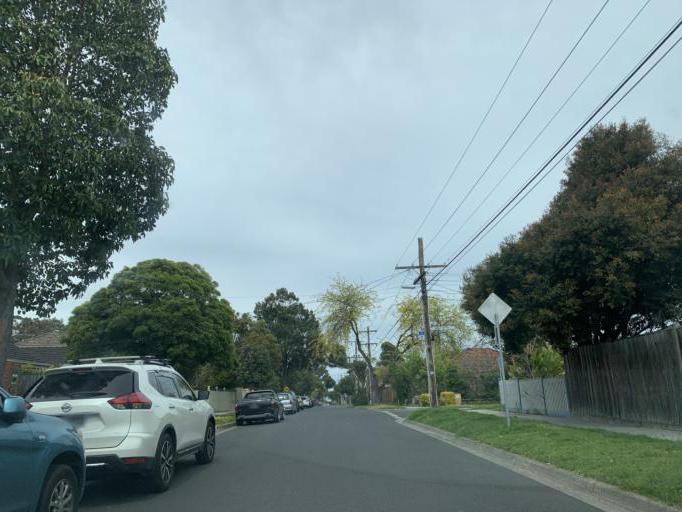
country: AU
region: Victoria
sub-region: Bayside
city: Highett
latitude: -37.9522
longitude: 145.0390
